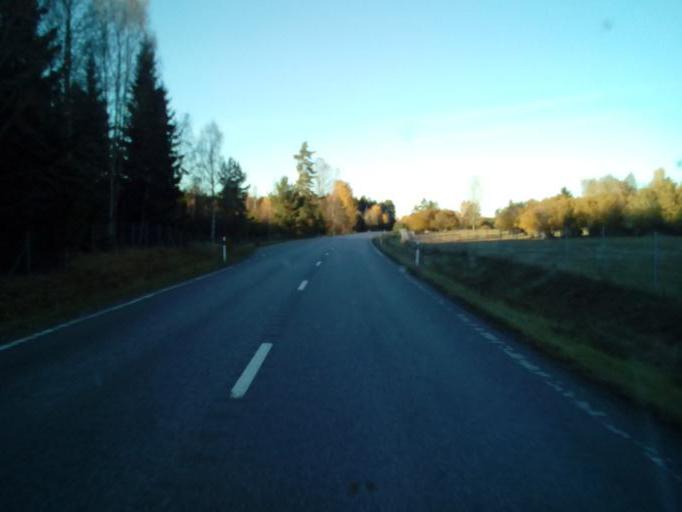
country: SE
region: OErebro
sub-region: Hallsbergs Kommun
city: Palsboda
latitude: 58.9842
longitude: 15.4090
